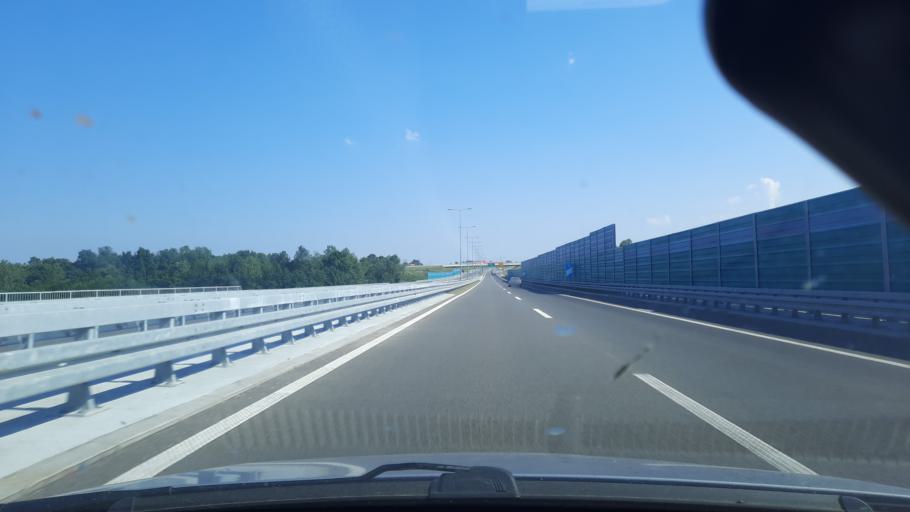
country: RS
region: Central Serbia
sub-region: Kolubarski Okrug
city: Ub
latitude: 44.4627
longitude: 20.1215
